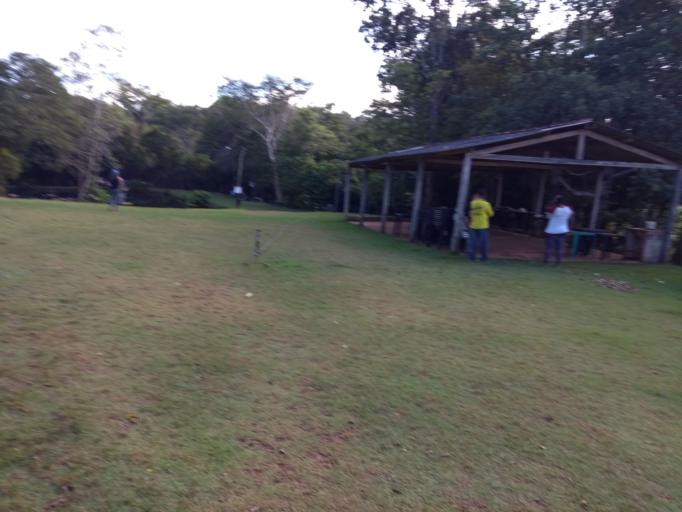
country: BR
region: Goias
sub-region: Goianesia
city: Goianesia
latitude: -15.5106
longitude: -48.9535
